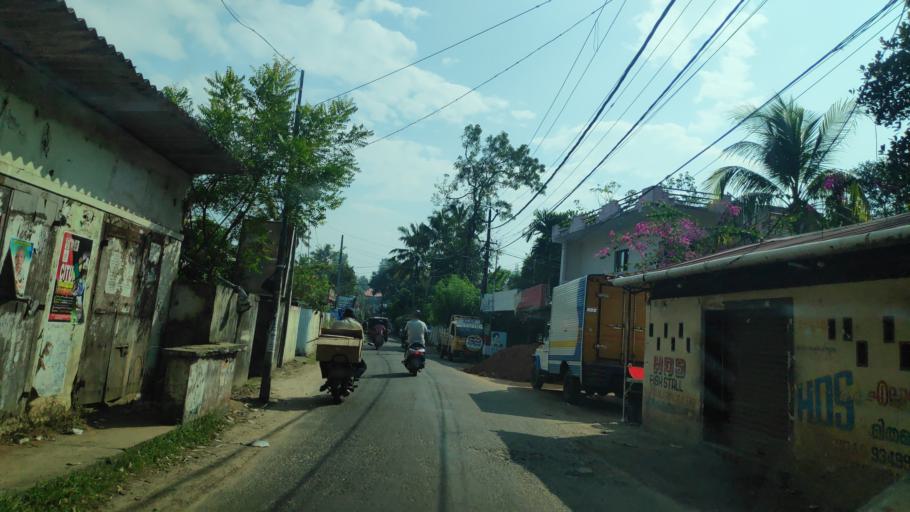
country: IN
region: Kerala
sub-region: Alappuzha
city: Alleppey
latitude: 9.5076
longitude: 76.3203
